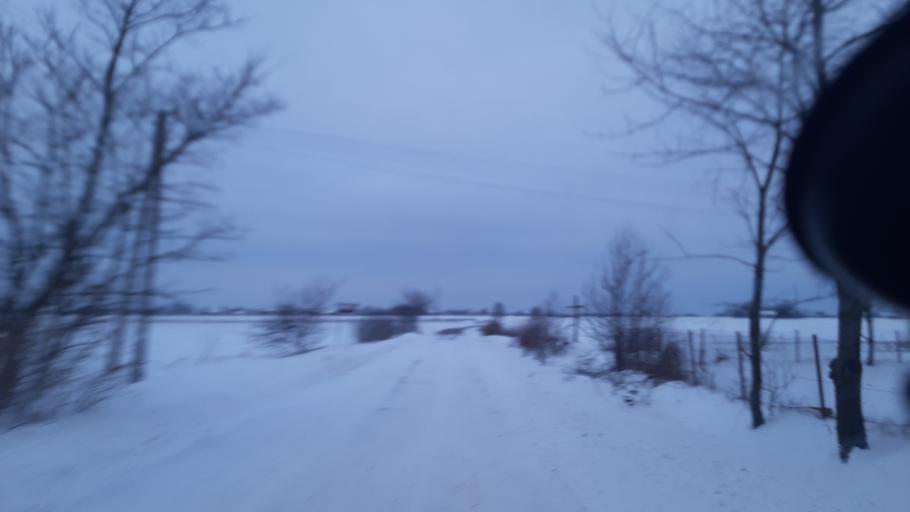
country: PL
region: Lublin Voivodeship
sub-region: Powiat lubelski
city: Jastkow
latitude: 51.3466
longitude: 22.4090
